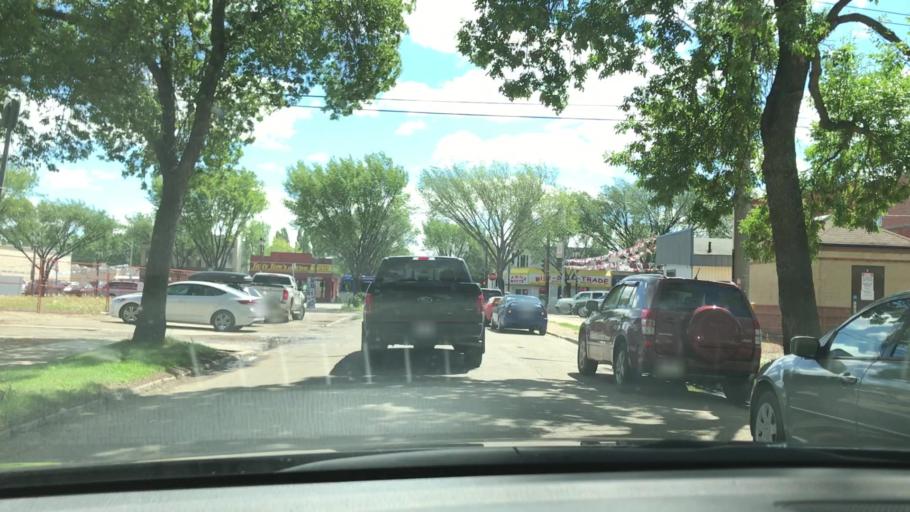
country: CA
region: Alberta
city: Edmonton
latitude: 53.5189
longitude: -113.4886
